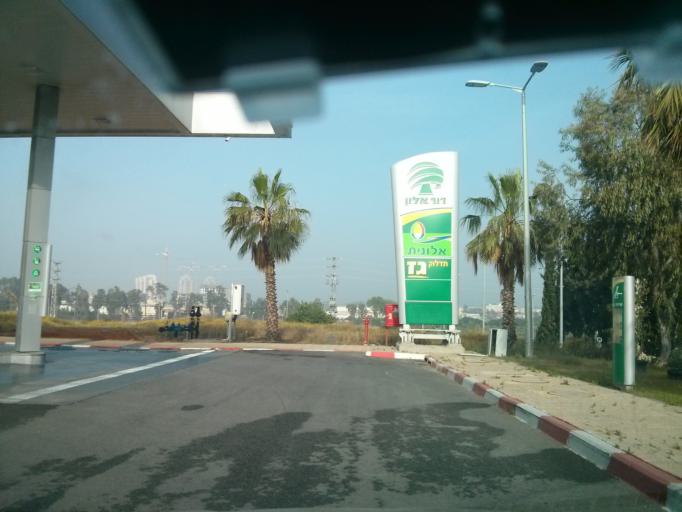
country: IL
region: Haifa
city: Qesarya
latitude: 32.5083
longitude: 34.9321
